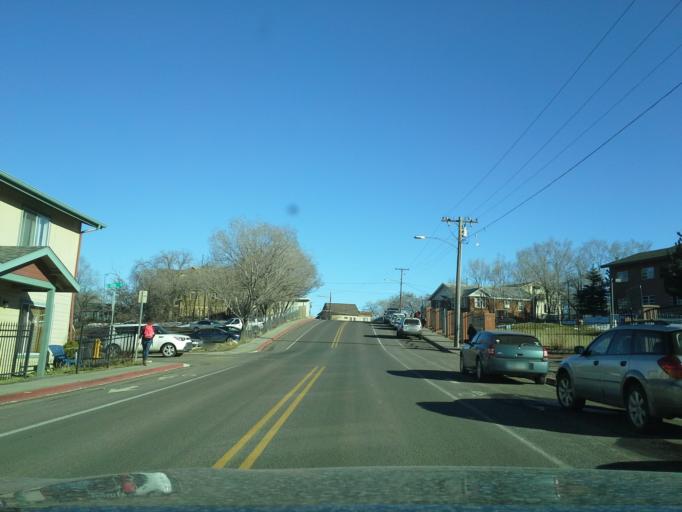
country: US
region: Arizona
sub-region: Coconino County
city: Flagstaff
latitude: 35.1903
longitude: -111.6493
